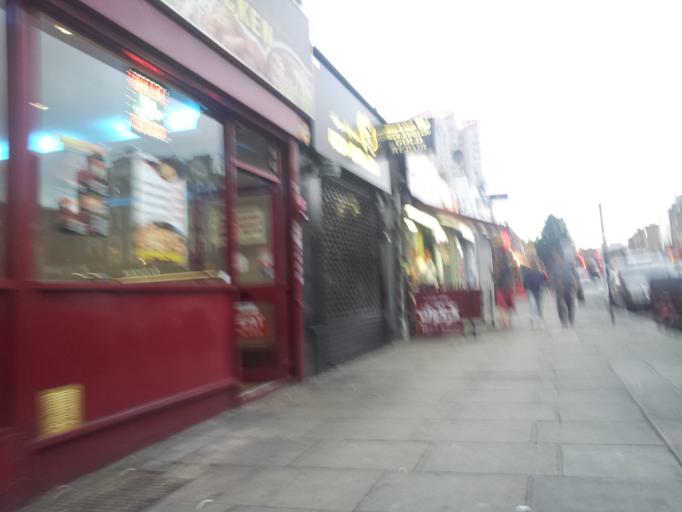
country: GB
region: England
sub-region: Greater London
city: Bayswater
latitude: 51.5222
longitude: -0.1735
